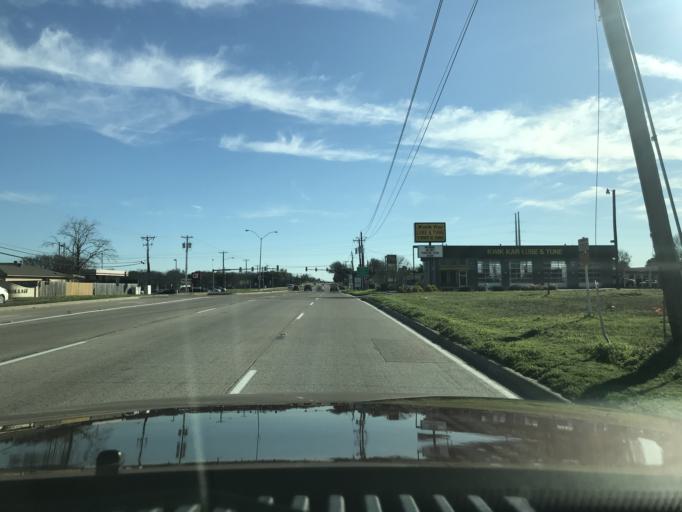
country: US
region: Texas
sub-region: Tarrant County
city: Edgecliff Village
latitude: 32.6505
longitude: -97.3486
